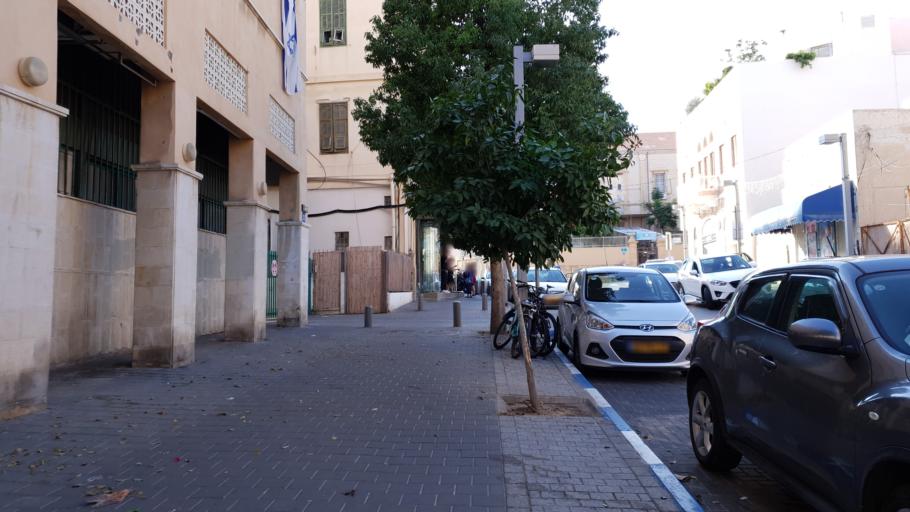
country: IL
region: Tel Aviv
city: Yafo
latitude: 32.0509
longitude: 34.7535
